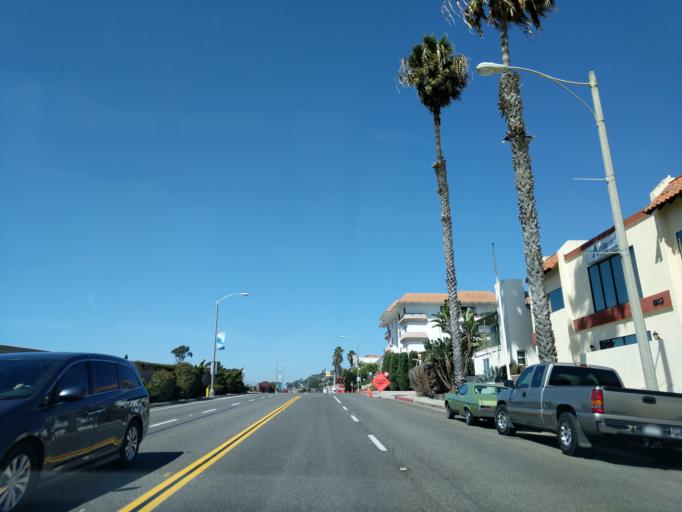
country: US
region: California
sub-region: Orange County
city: San Clemente
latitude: 33.4081
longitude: -117.5993
